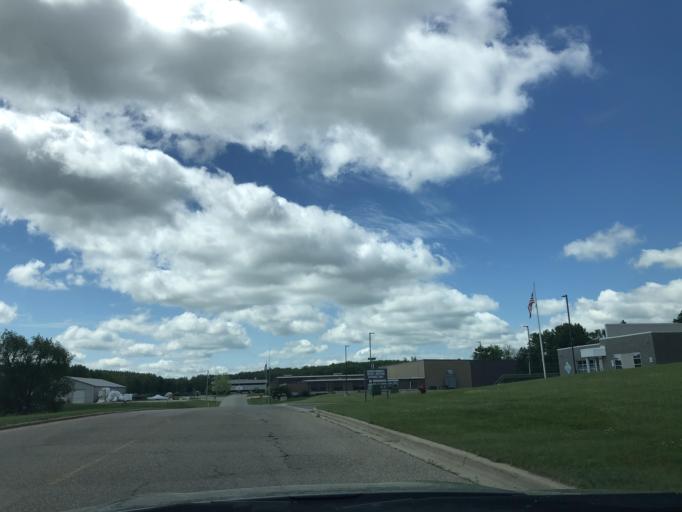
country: US
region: Michigan
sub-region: Clare County
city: Harrison
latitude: 44.0183
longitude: -84.8118
